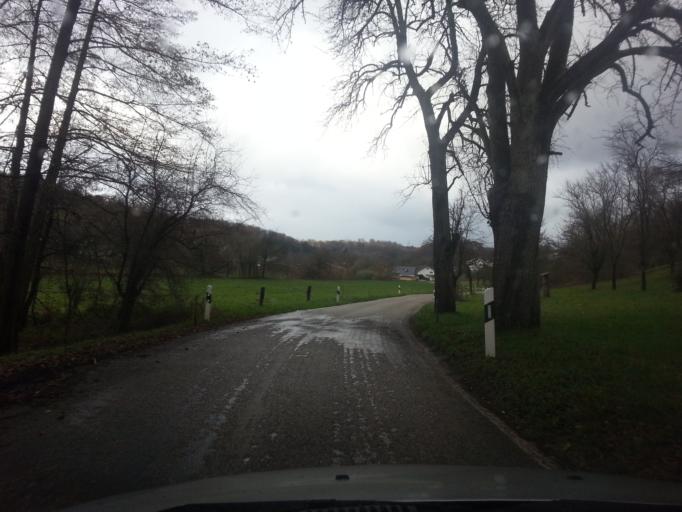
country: DE
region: Baden-Wuerttemberg
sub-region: Karlsruhe Region
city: Nussloch
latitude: 49.3251
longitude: 8.7342
